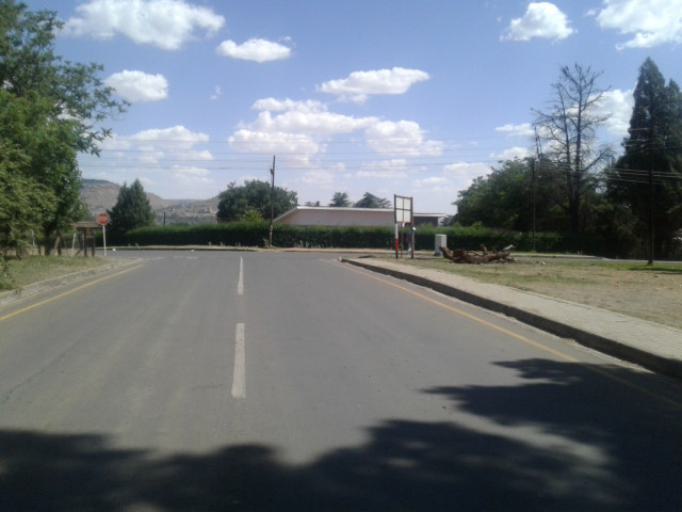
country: LS
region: Maseru
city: Maseru
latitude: -29.3057
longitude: 27.4718
